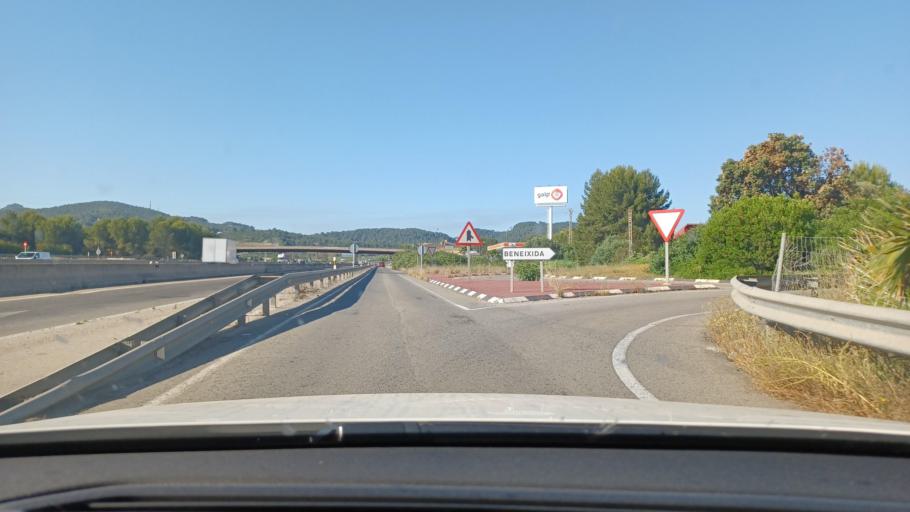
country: ES
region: Valencia
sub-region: Provincia de Valencia
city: Beneixida
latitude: 39.0610
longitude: -0.5438
